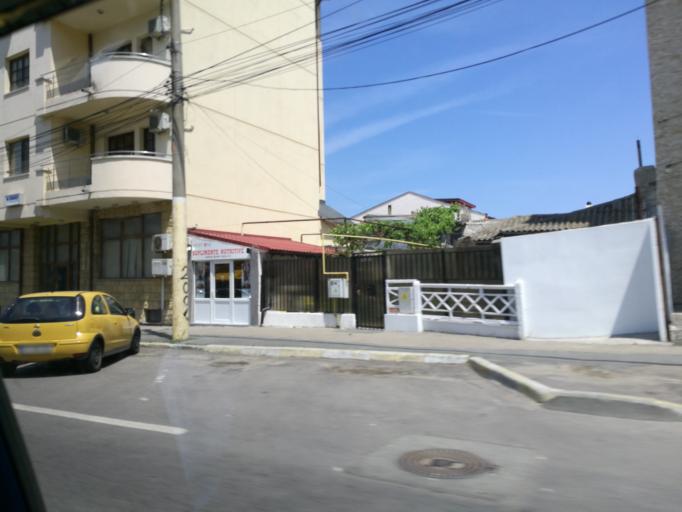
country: RO
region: Constanta
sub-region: Municipiul Constanta
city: Constanta
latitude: 44.2007
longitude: 28.6466
